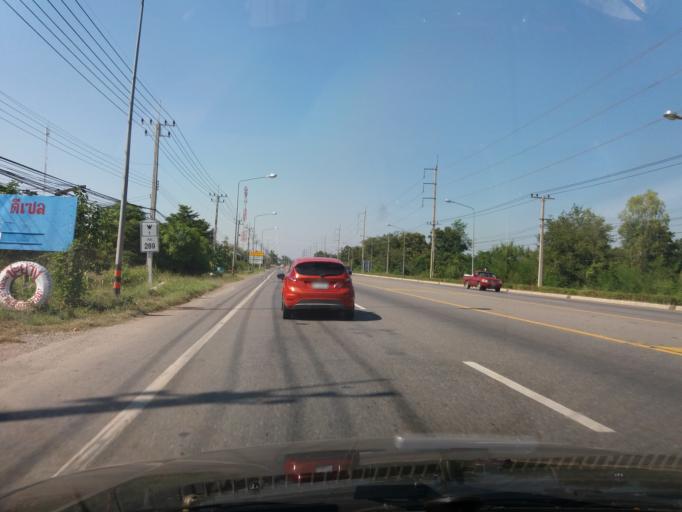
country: TH
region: Chai Nat
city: Wat Sing
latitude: 15.2562
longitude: 100.0952
